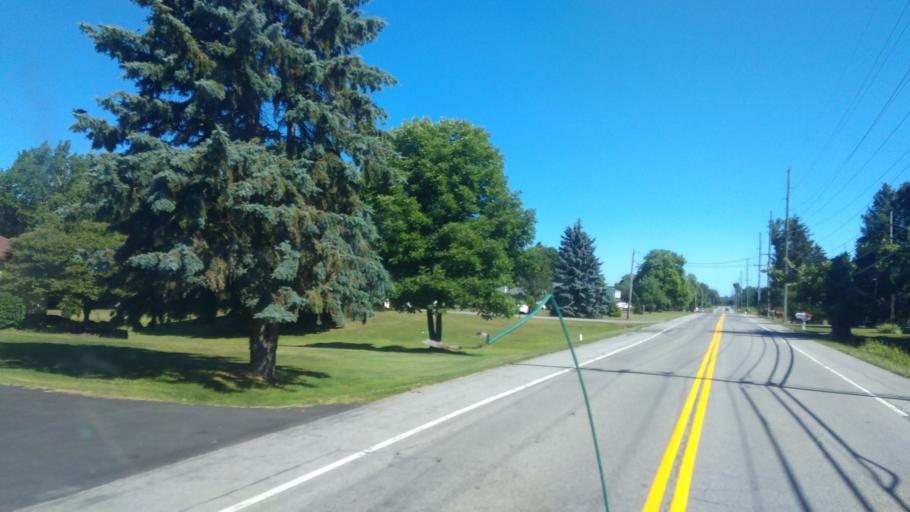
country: US
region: New York
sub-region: Monroe County
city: Webster
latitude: 43.2551
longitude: -77.4008
